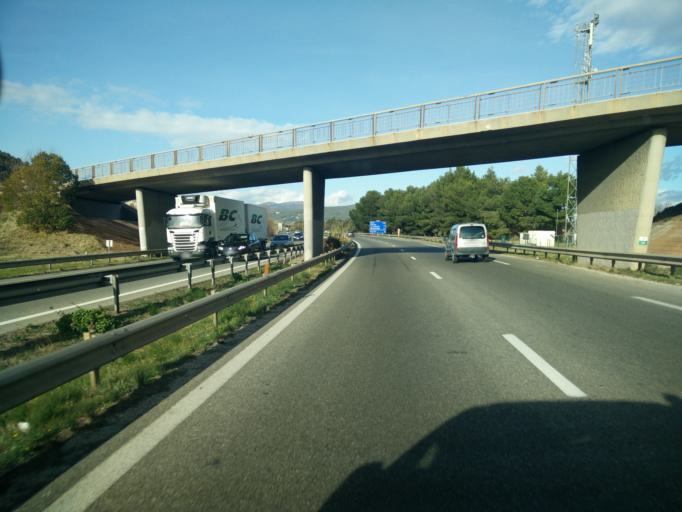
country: FR
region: Provence-Alpes-Cote d'Azur
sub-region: Departement du Var
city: La Farlede
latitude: 43.1652
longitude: 6.0517
